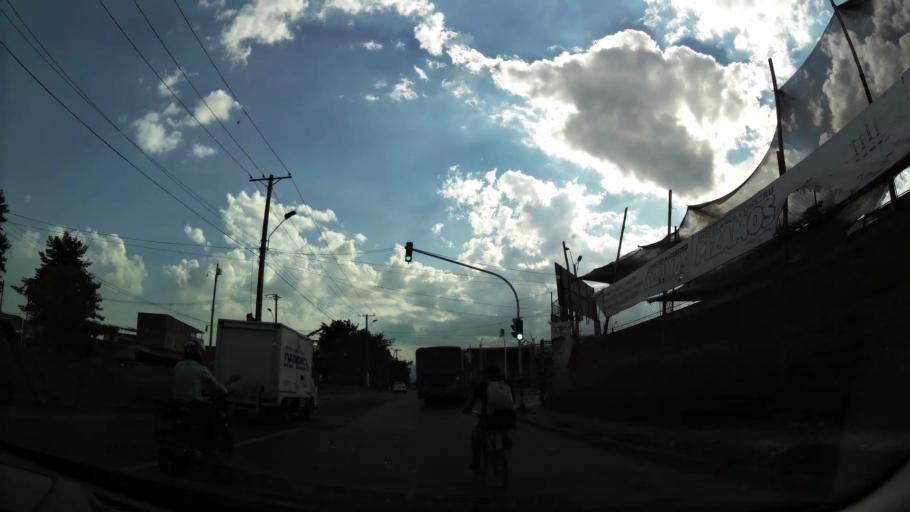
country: CO
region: Valle del Cauca
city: Cali
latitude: 3.4130
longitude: -76.4911
